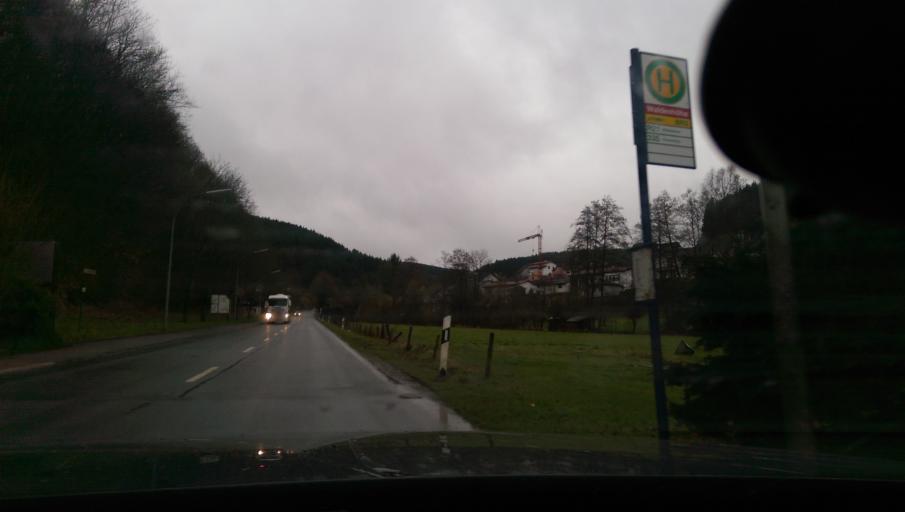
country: DE
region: North Rhine-Westphalia
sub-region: Regierungsbezirk Arnsberg
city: Sundern
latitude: 51.2590
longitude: 7.9652
